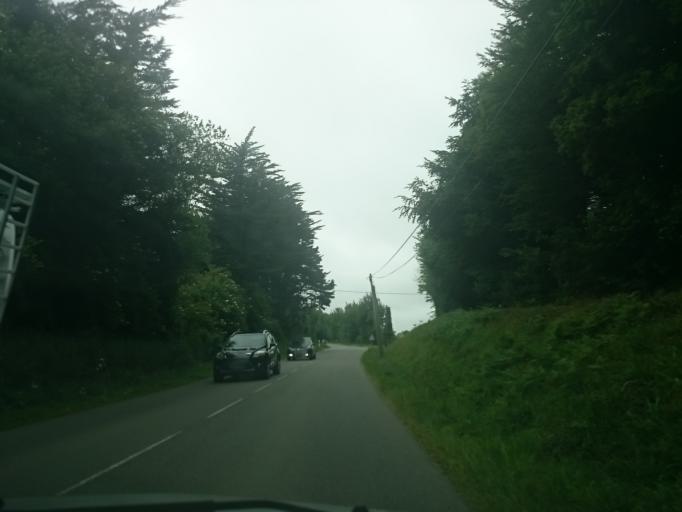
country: FR
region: Brittany
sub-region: Departement du Finistere
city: Lannilis
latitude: 48.5533
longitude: -4.5489
